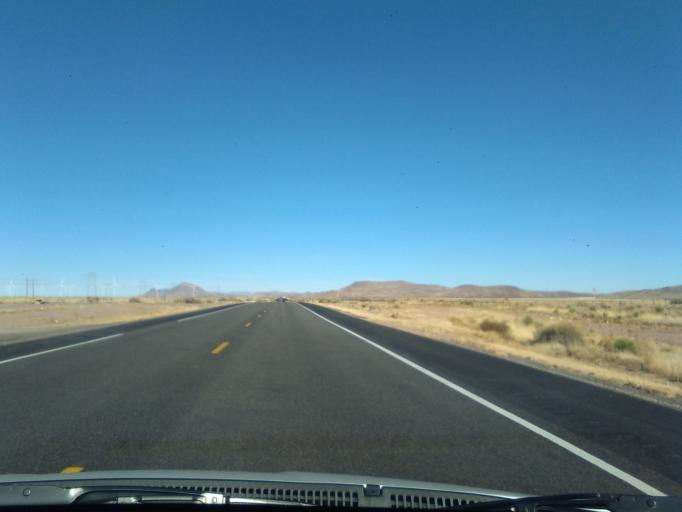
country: US
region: New Mexico
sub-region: Luna County
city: Deming
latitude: 32.4935
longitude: -107.5181
